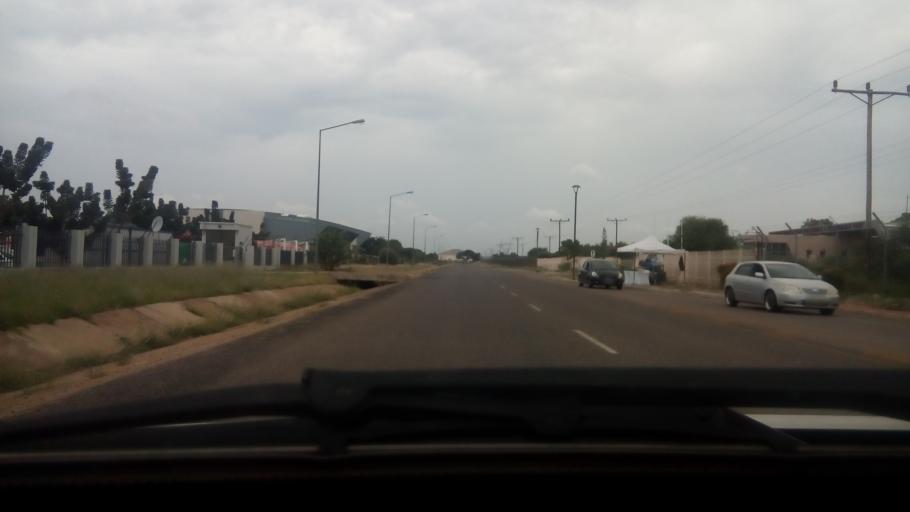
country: BW
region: Kweneng
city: Mmopone
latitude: -24.5888
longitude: 25.9110
